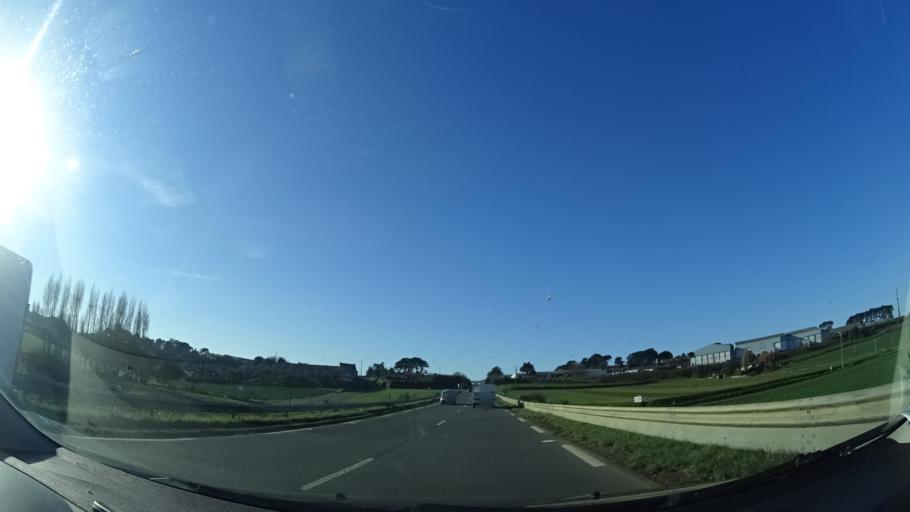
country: FR
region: Brittany
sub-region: Departement du Finistere
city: Saint-Pol-de-Leon
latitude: 48.6648
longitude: -3.9753
